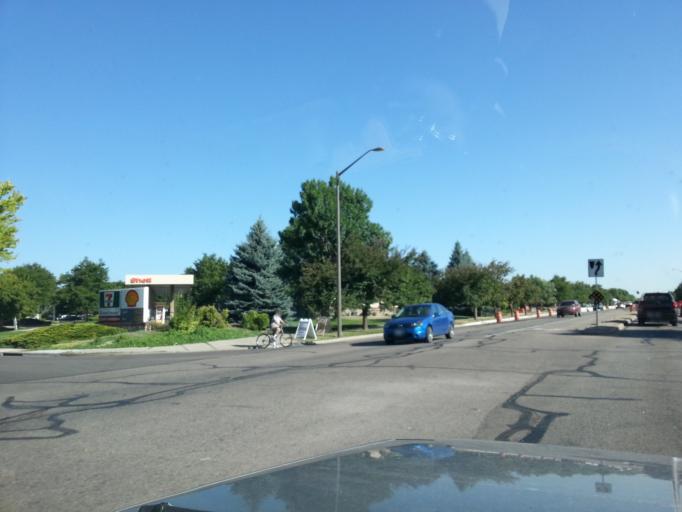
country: US
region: Colorado
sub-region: Larimer County
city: Fort Collins
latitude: 40.5353
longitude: -105.0393
